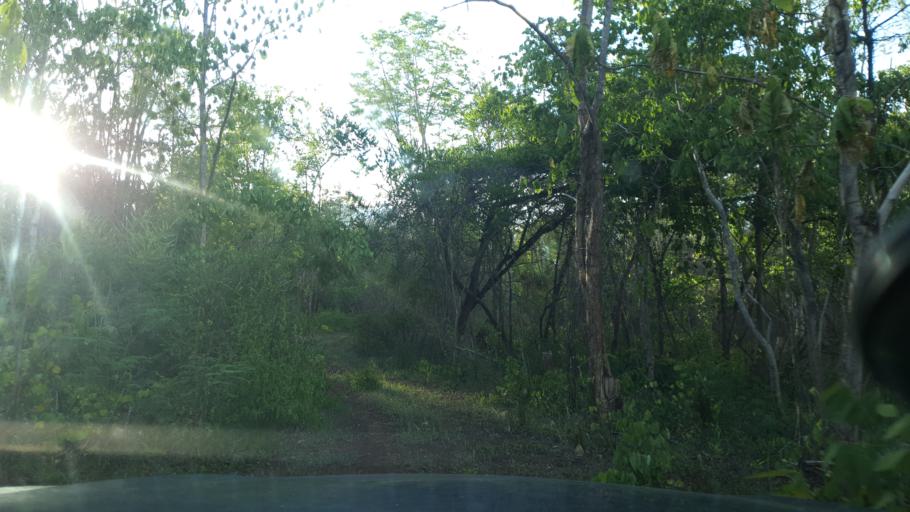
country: TH
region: Lampang
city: Sop Prap
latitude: 17.9647
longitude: 99.3517
